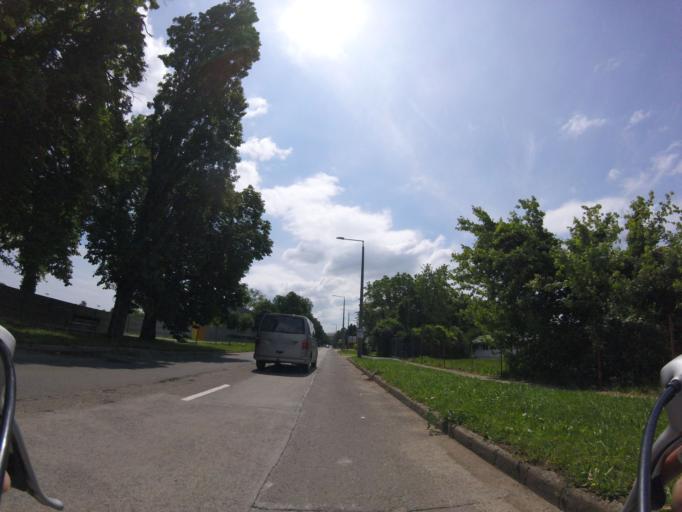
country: HU
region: Baranya
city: Siklos
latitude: 45.8628
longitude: 18.2869
